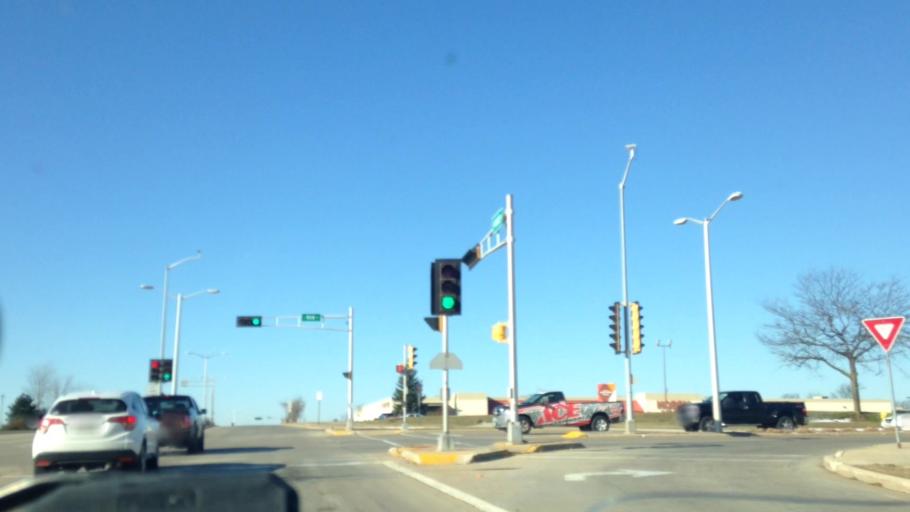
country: US
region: Wisconsin
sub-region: Washington County
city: West Bend
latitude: 43.3978
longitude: -88.1805
